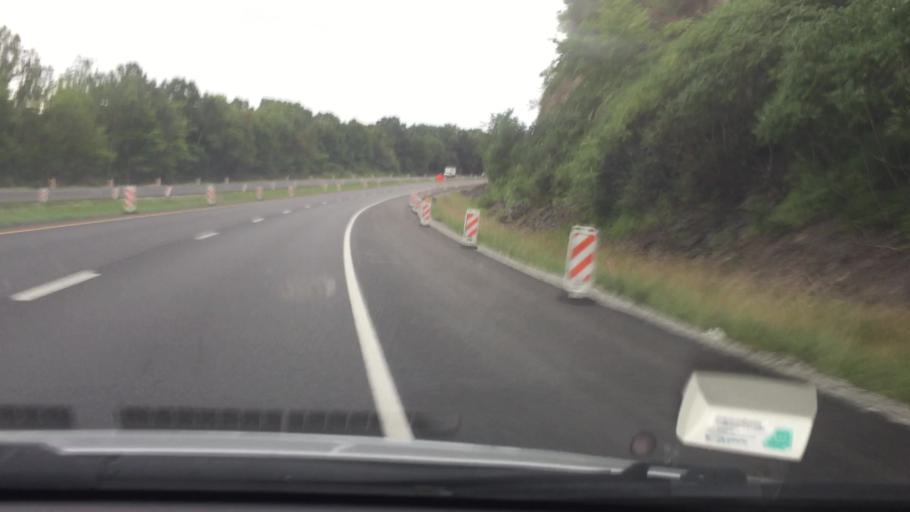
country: US
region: Pennsylvania
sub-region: Allegheny County
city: Brackenridge
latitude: 40.6449
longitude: -79.7203
